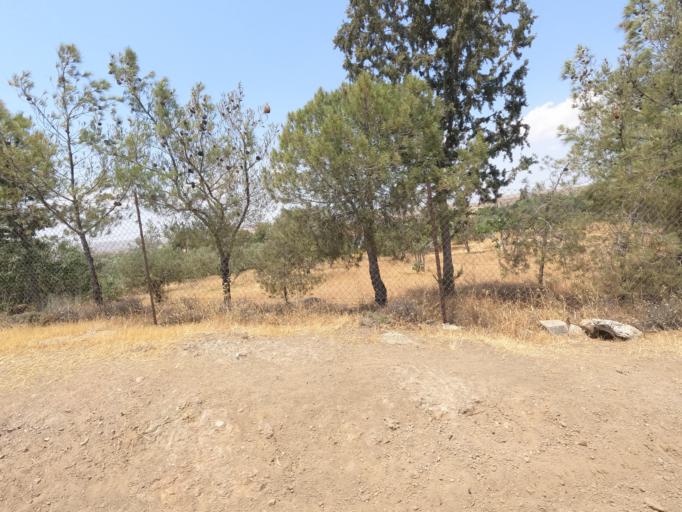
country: CY
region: Larnaka
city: Troulloi
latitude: 35.0154
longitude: 33.6059
